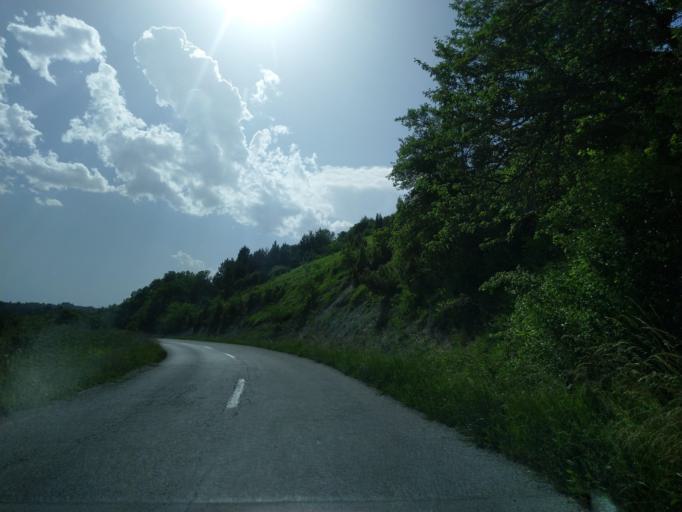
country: RS
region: Central Serbia
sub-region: Zlatiborski Okrug
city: Bajina Basta
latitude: 43.8459
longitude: 19.6128
